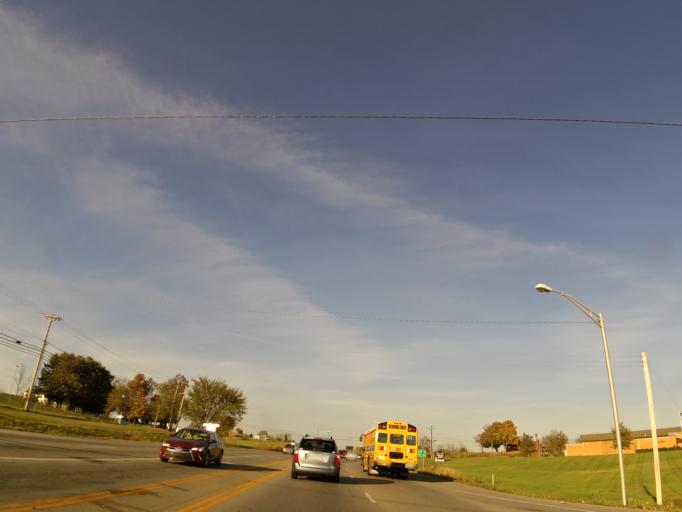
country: US
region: Kentucky
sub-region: Lincoln County
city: Stanford
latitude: 37.5411
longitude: -84.6520
